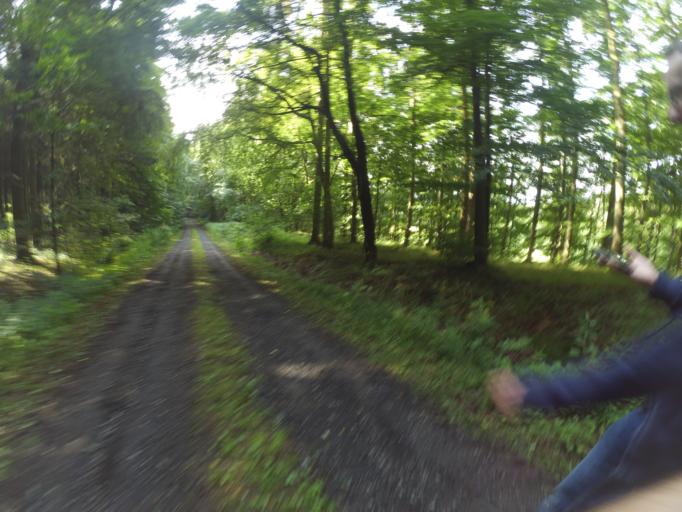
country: DE
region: Hesse
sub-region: Regierungsbezirk Kassel
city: Kirchheim
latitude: 50.8798
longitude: 9.5275
